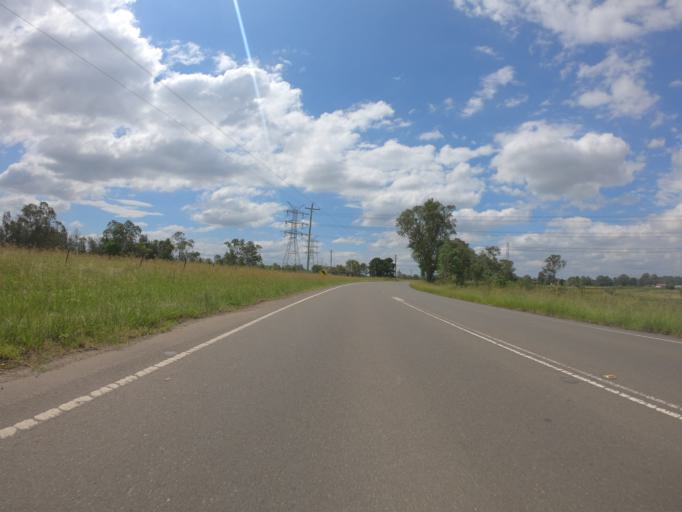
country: AU
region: New South Wales
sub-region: Penrith Municipality
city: Kingswood Park
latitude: -33.8133
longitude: 150.7602
